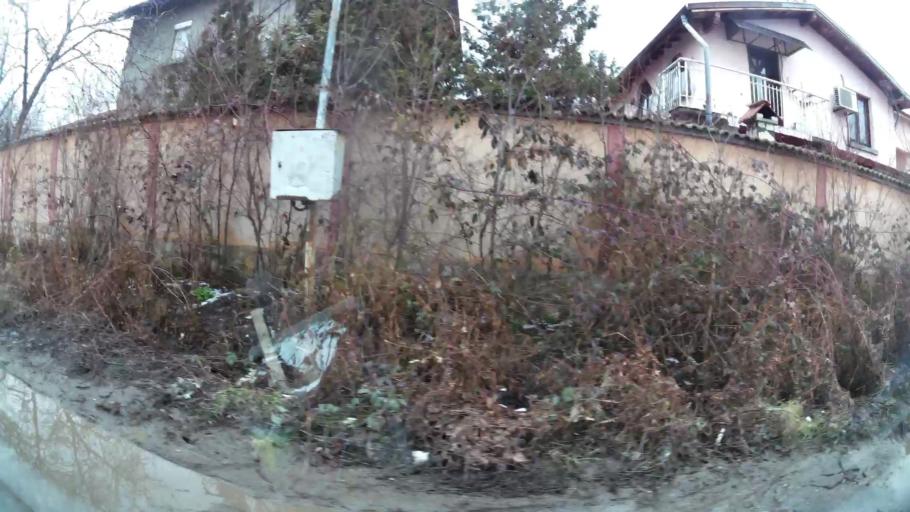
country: BG
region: Sofia-Capital
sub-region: Stolichna Obshtina
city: Sofia
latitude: 42.7246
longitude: 23.2793
